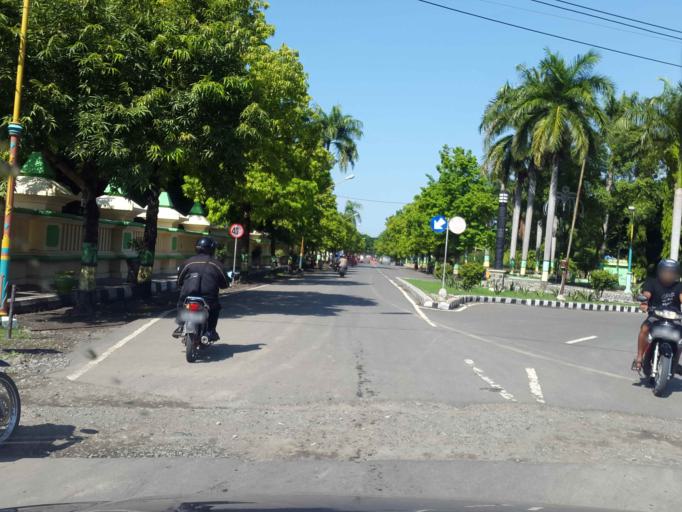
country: ID
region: Central Java
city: Slawi
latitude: -6.9938
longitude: 109.1297
